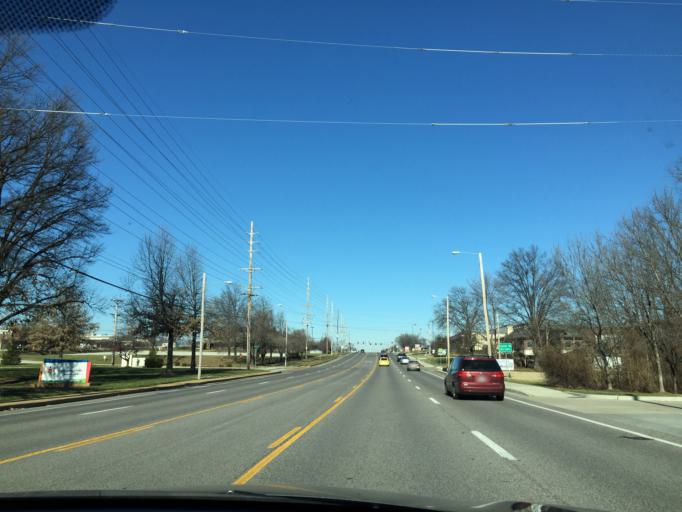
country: US
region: Missouri
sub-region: Saint Louis County
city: Ellisville
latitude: 38.6016
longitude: -90.5856
